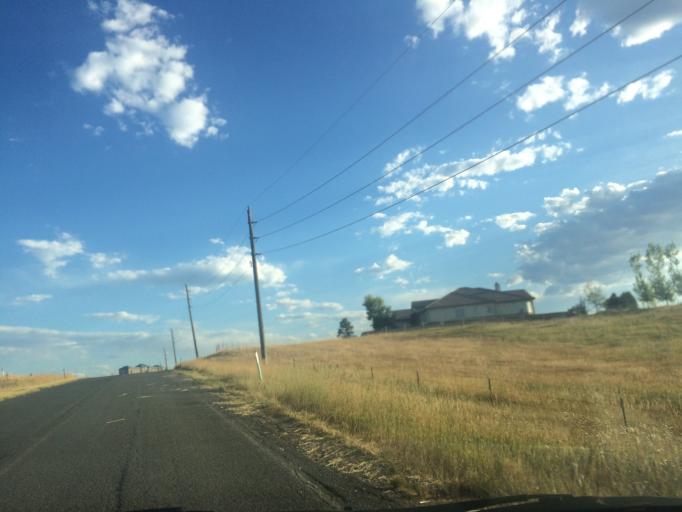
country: US
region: Colorado
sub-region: Broomfield County
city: Broomfield
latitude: 39.9380
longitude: -105.1188
